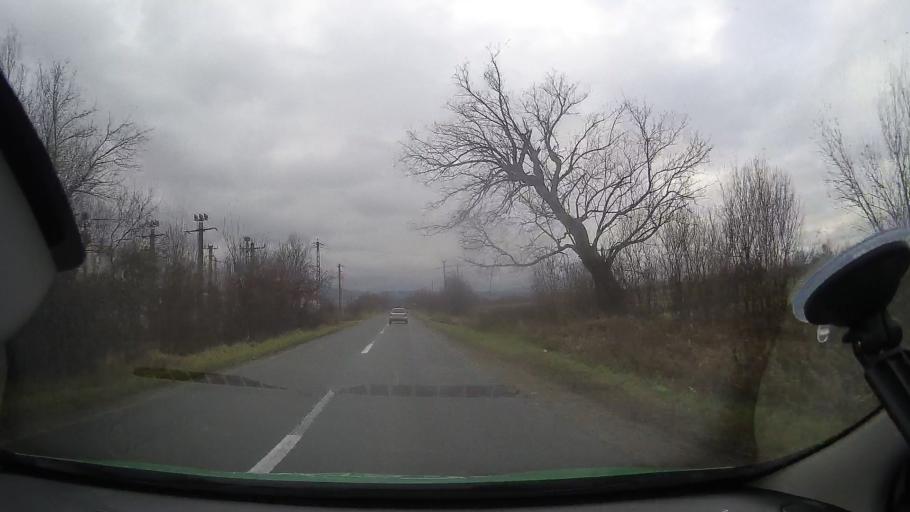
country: RO
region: Arad
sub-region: Comuna Sebis
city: Sebis
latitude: 46.3536
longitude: 22.1304
